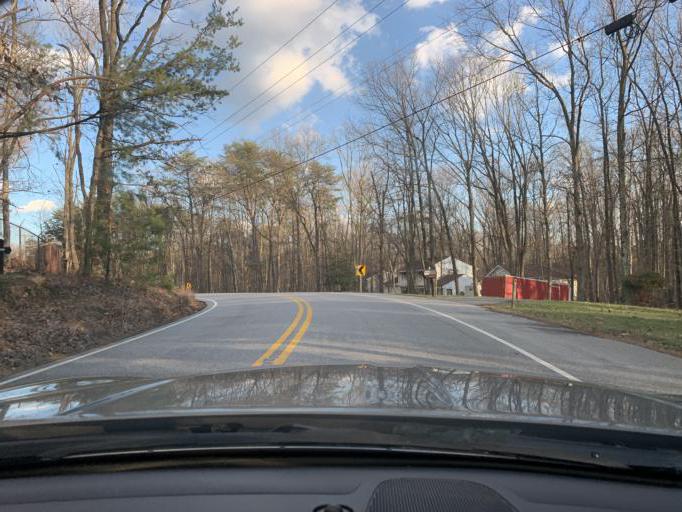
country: US
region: Maryland
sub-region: Anne Arundel County
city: Gambrills
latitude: 39.0848
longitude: -76.6657
